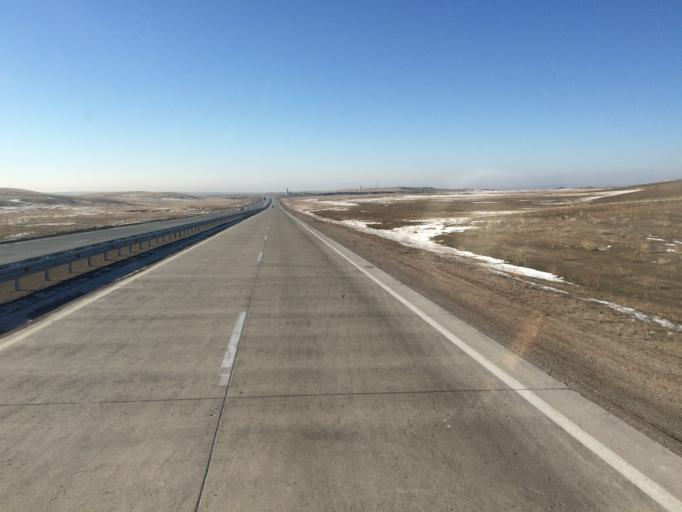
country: KZ
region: Zhambyl
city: Georgiyevka
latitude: 43.3565
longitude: 74.5859
